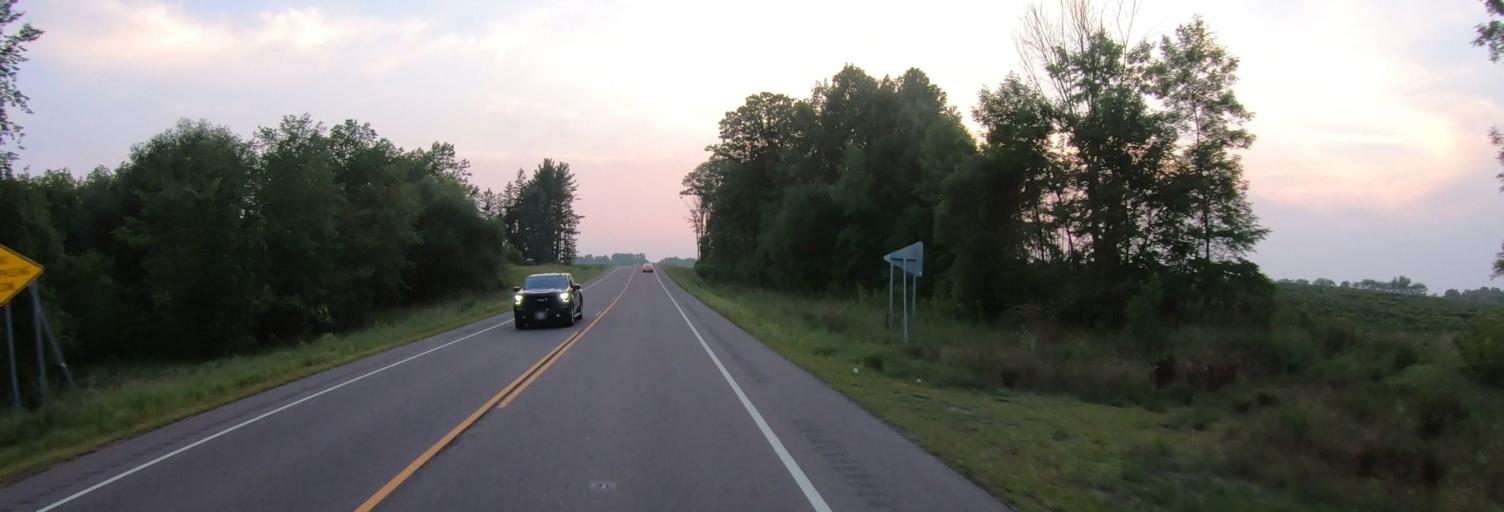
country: US
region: Minnesota
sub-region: Pine County
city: Rock Creek
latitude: 45.7735
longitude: -92.9192
